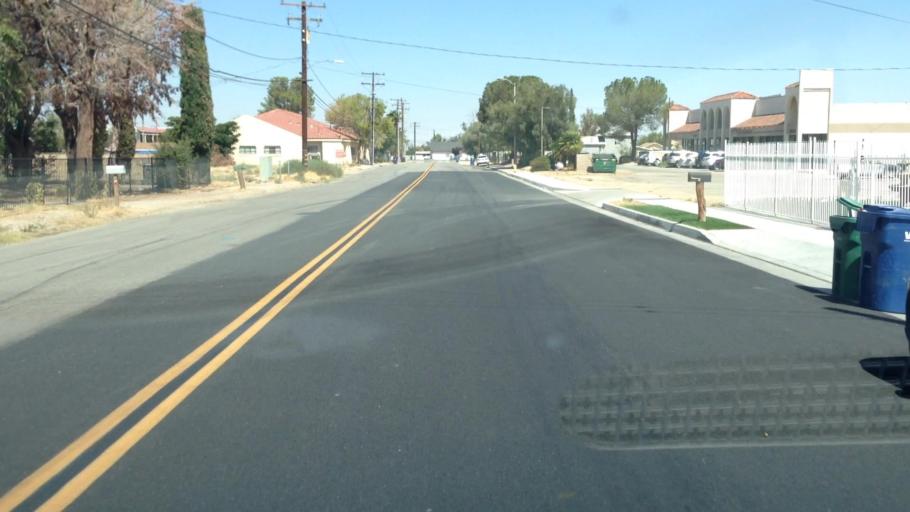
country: US
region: California
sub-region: Los Angeles County
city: Palmdale
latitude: 34.5844
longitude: -118.1144
